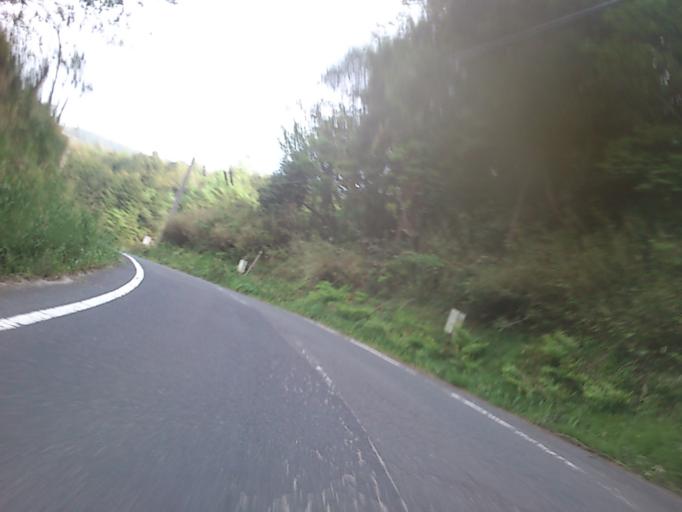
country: JP
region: Kyoto
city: Miyazu
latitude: 35.5731
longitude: 135.1123
